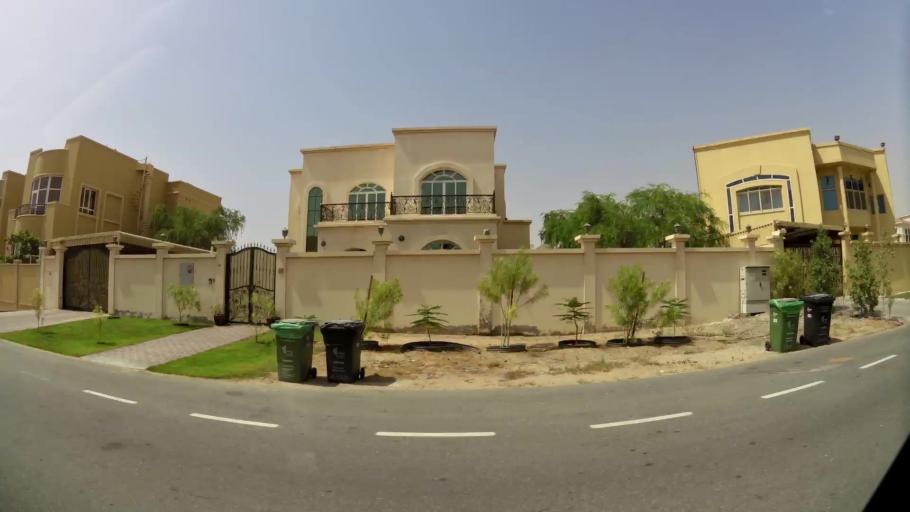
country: AE
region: Ash Shariqah
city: Sharjah
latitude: 25.2389
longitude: 55.4385
